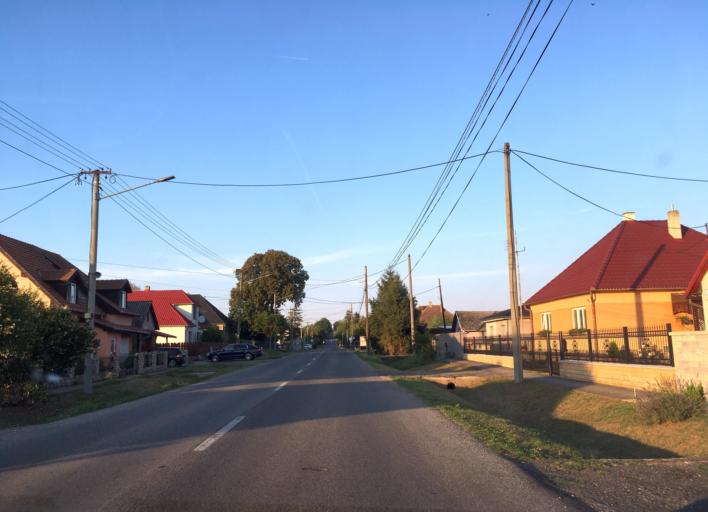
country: HU
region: Komarom-Esztergom
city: Dunaalmas
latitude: 47.8033
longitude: 18.3234
